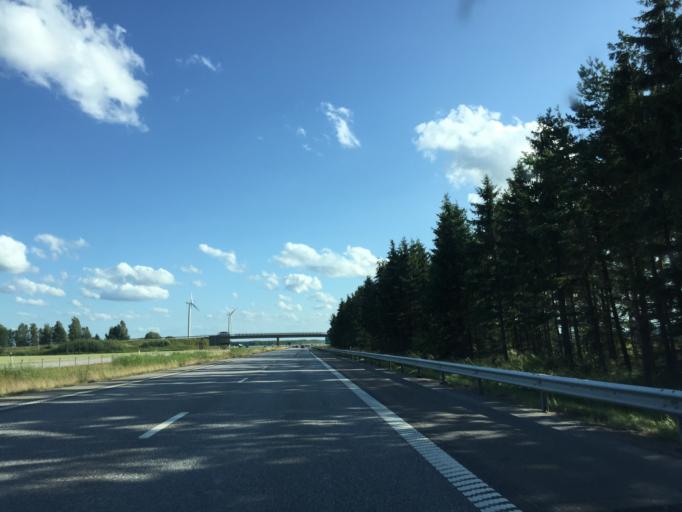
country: SE
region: OErebro
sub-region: Kumla Kommun
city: Kumla
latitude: 59.1986
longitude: 15.1260
